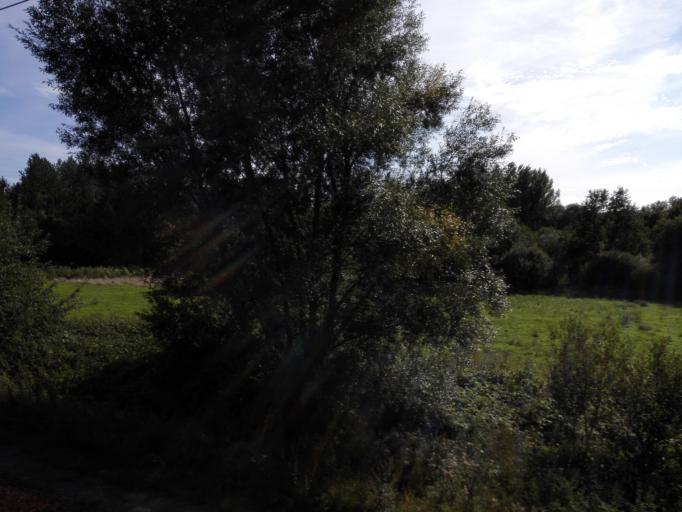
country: BE
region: Flanders
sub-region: Provincie Vlaams-Brabant
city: Herent
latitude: 50.9385
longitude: 4.6738
